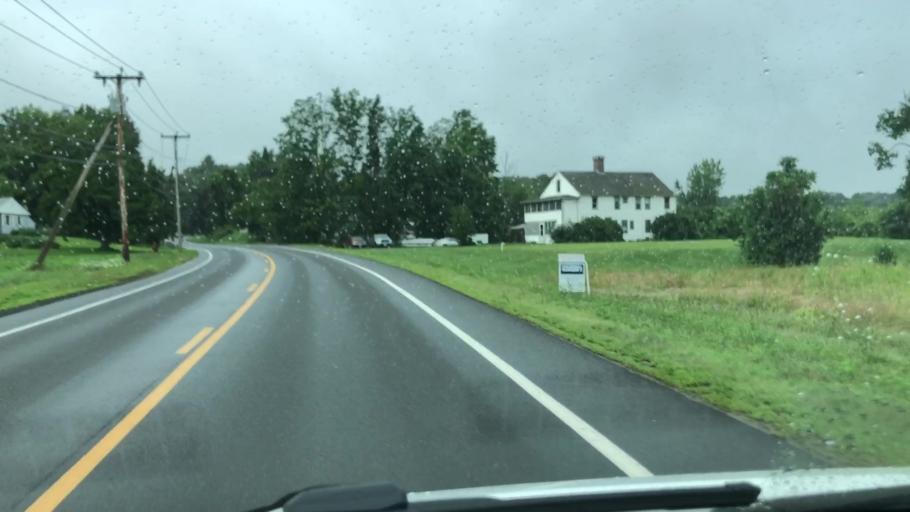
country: US
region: Massachusetts
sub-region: Franklin County
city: South Deerfield
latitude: 42.5196
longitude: -72.6067
